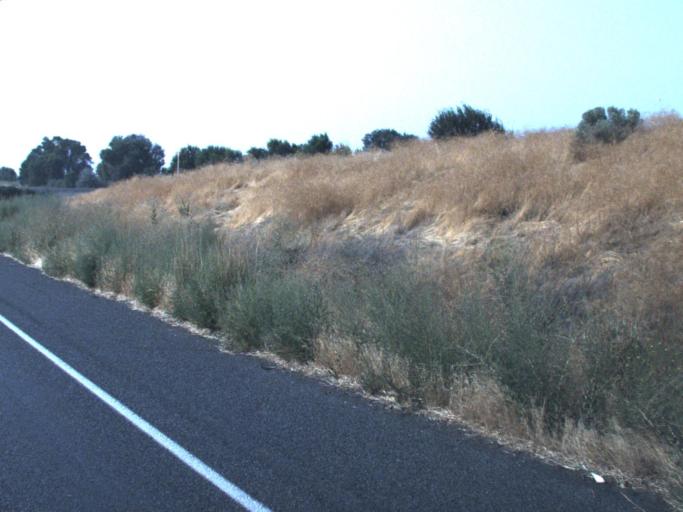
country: US
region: Washington
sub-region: Yakima County
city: Mabton
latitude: 46.2158
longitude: -120.0168
